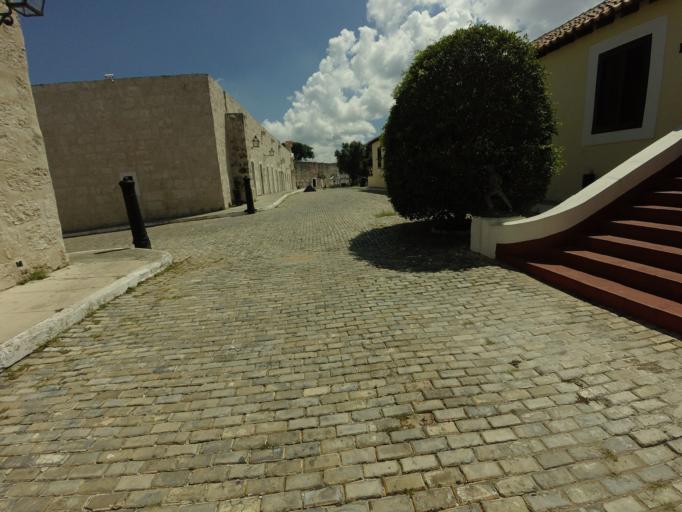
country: CU
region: La Habana
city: Centro Habana
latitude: 23.1470
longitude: -82.3504
